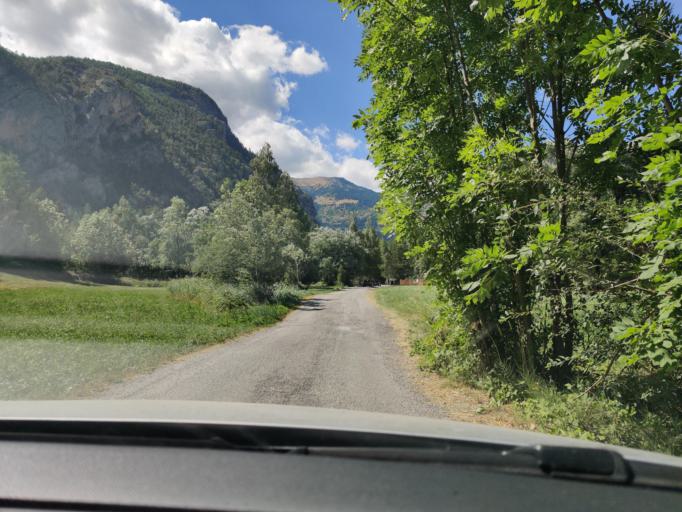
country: FR
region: Provence-Alpes-Cote d'Azur
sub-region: Departement des Hautes-Alpes
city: Saint-Martin-de-Queyrieres
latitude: 44.7405
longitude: 6.5628
